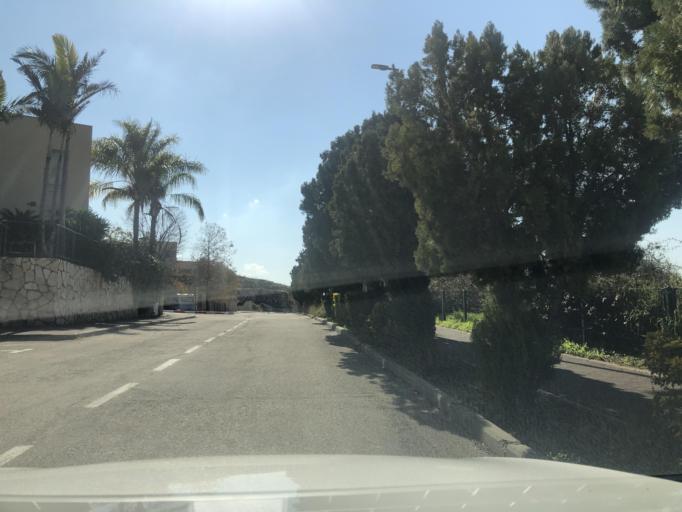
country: PS
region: West Bank
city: Mashah
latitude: 32.1104
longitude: 35.0368
